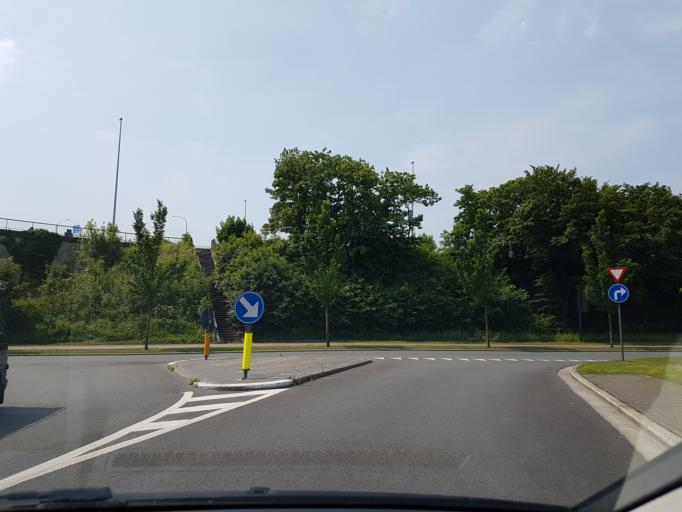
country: BE
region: Flanders
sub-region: Provincie Oost-Vlaanderen
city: Aalst
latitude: 50.9490
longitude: 4.0310
